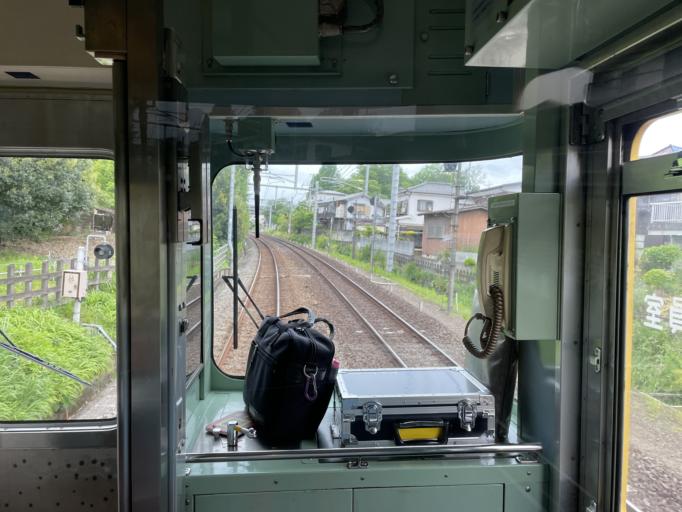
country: JP
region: Saitama
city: Hanno
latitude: 35.8420
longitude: 139.3410
